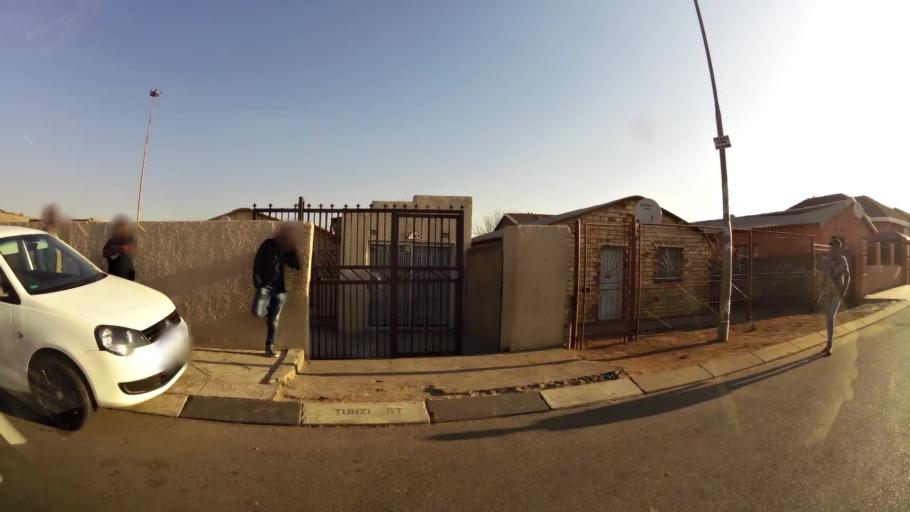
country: ZA
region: Gauteng
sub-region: City of Johannesburg Metropolitan Municipality
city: Soweto
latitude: -26.2591
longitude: 27.8798
